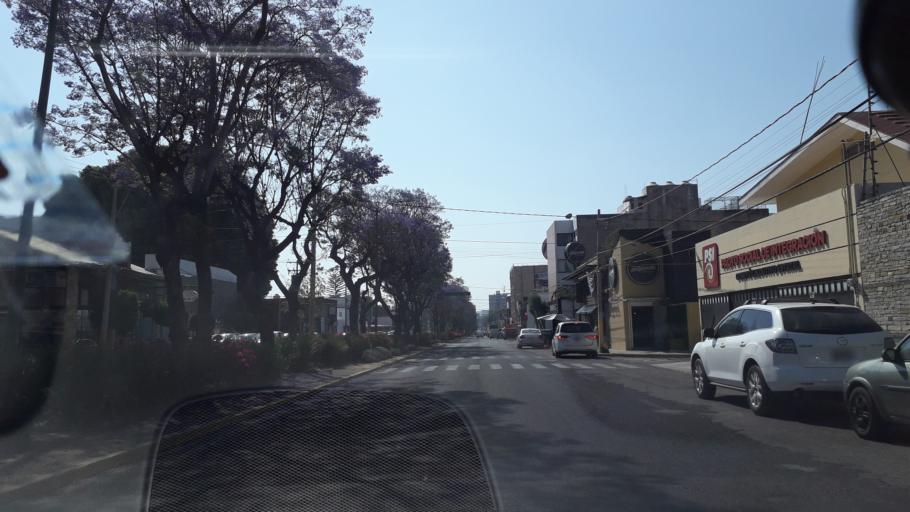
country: MX
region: Puebla
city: Puebla
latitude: 19.0306
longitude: -98.2137
